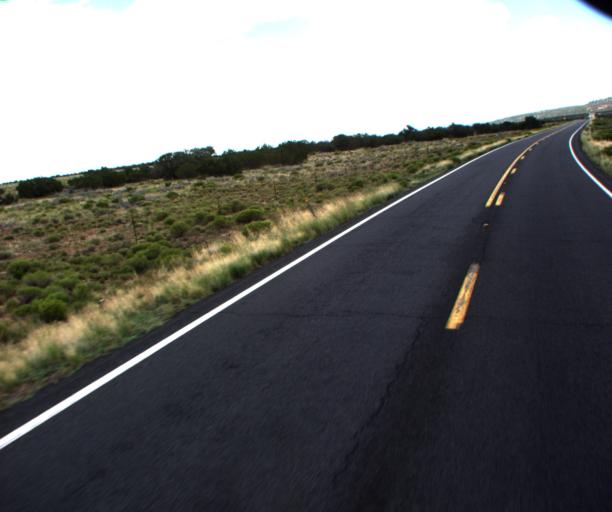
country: US
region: Arizona
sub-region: Coconino County
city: Parks
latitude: 35.5776
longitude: -111.9376
